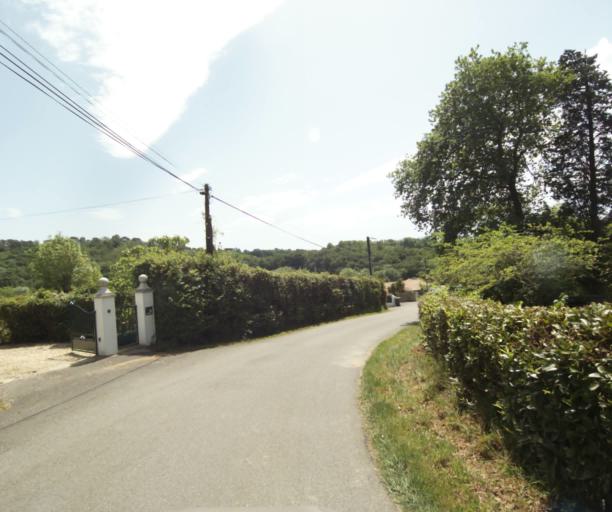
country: FR
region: Aquitaine
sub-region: Departement des Pyrenees-Atlantiques
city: Mouguerre
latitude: 43.4546
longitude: -1.4323
